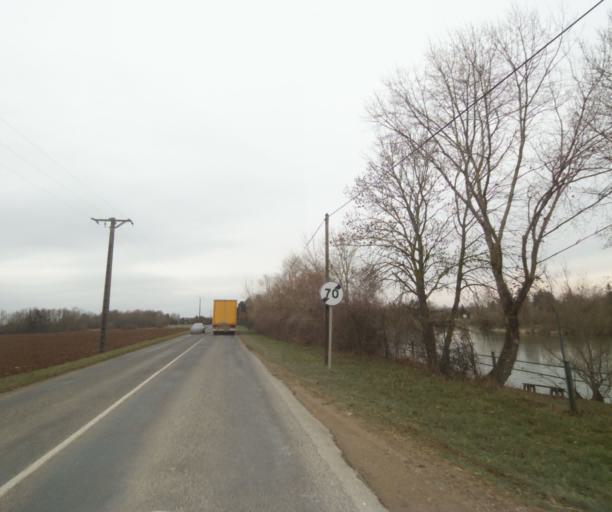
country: FR
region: Champagne-Ardenne
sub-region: Departement de la Haute-Marne
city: Villiers-en-Lieu
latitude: 48.6468
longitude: 4.9061
